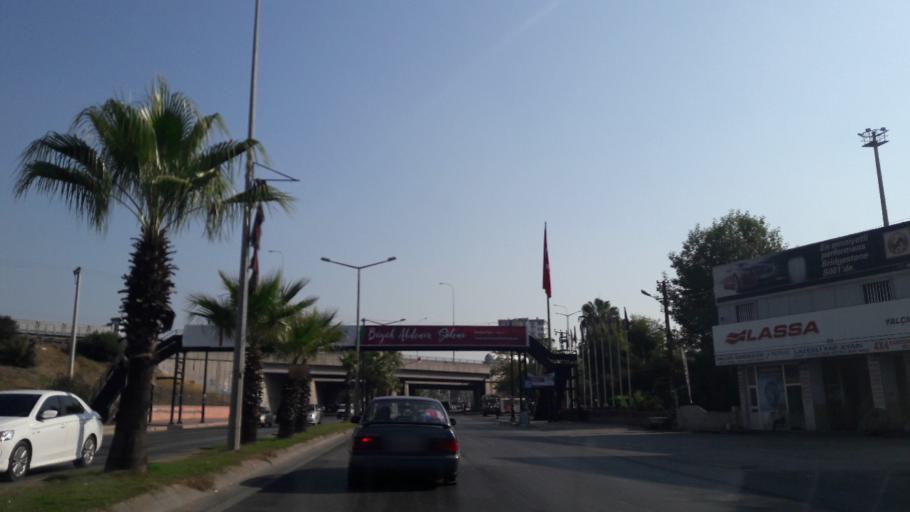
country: TR
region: Adana
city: Yuregir
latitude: 37.0284
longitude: 35.4036
